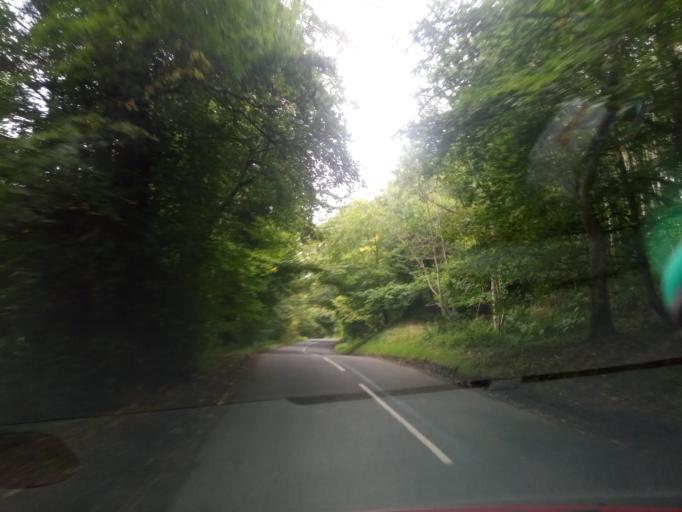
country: GB
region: Scotland
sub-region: The Scottish Borders
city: Duns
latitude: 55.8187
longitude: -2.3985
